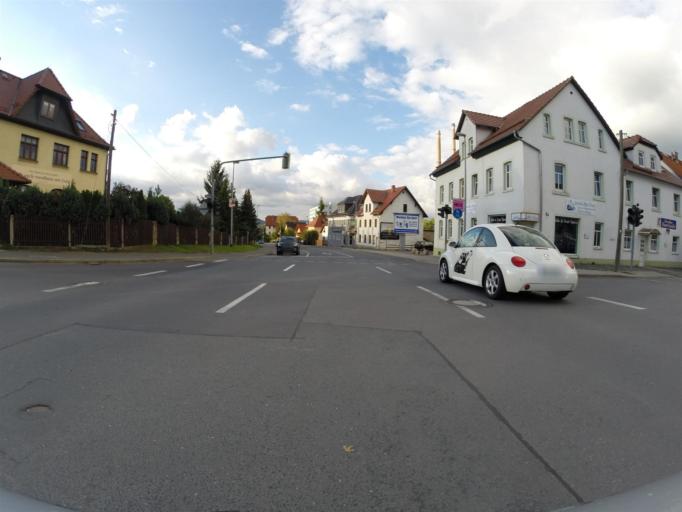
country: DE
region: Thuringia
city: Jena
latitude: 50.8927
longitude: 11.5849
